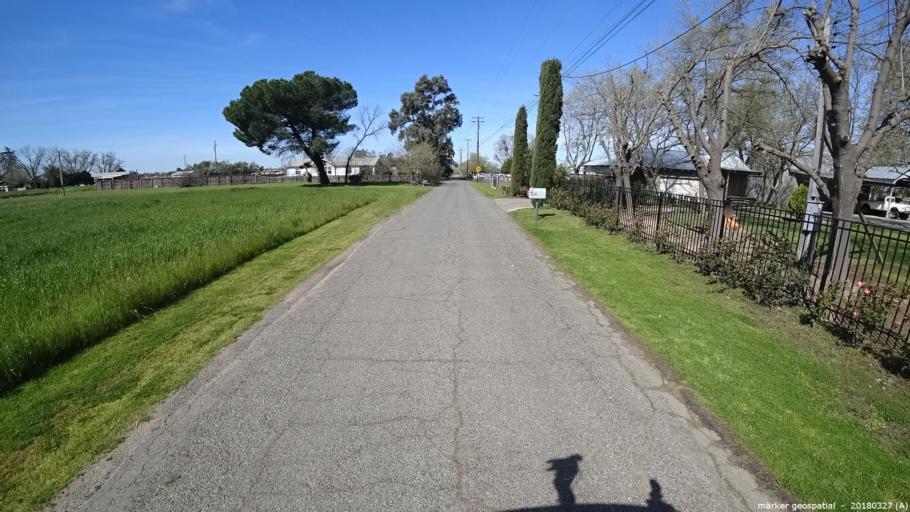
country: US
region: California
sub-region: Sacramento County
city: Florin
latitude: 38.5071
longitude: -121.3671
